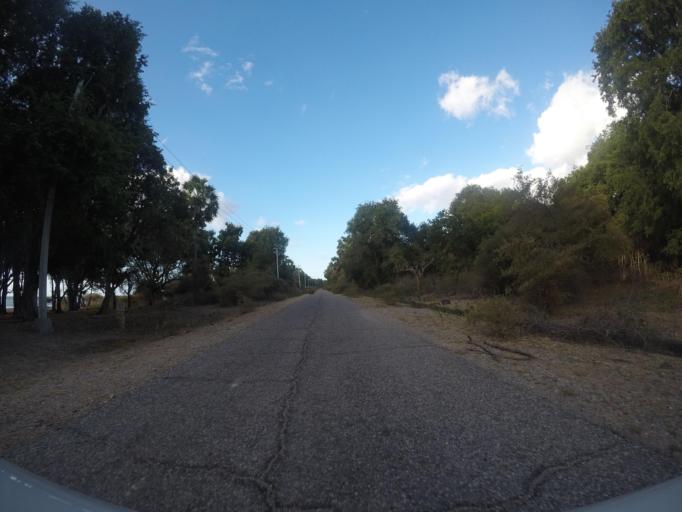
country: TL
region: Lautem
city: Lospalos
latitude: -8.3458
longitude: 126.9258
